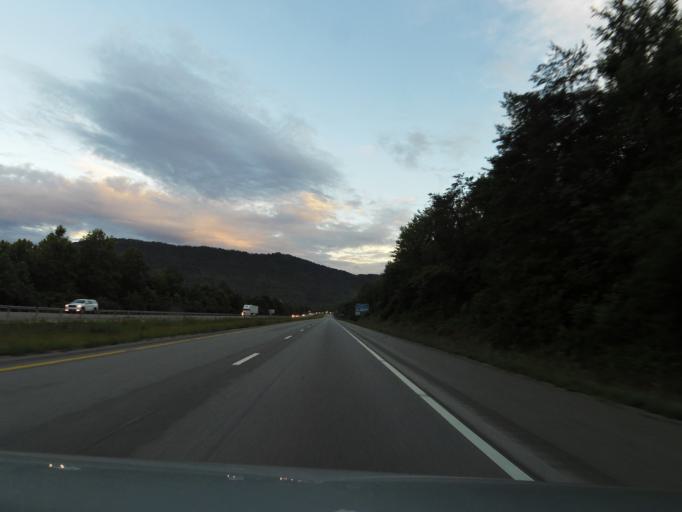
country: US
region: Tennessee
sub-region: Campbell County
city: Jellico
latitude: 36.6002
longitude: -84.1056
